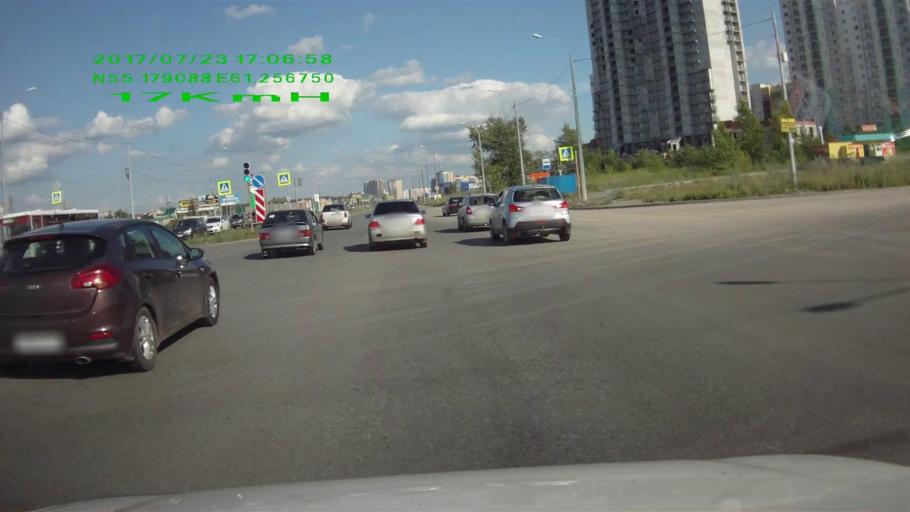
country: RU
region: Chelyabinsk
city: Roshchino
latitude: 55.1789
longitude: 61.2576
